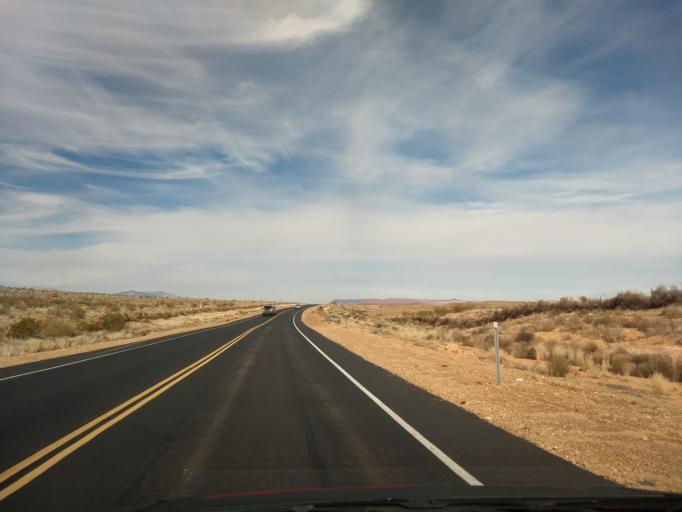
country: US
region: Utah
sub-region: Washington County
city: Washington
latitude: 37.0164
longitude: -113.4975
